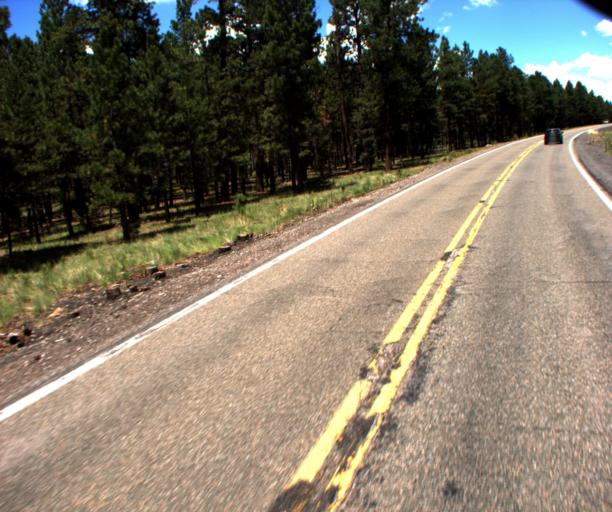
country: US
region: Arizona
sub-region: Coconino County
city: Flagstaff
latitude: 35.3135
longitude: -111.7752
